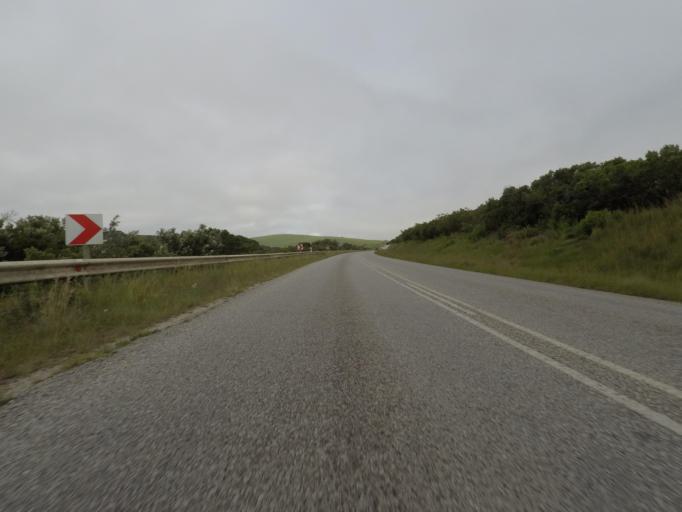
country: ZA
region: Eastern Cape
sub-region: Cacadu District Municipality
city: Port Alfred
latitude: -33.6100
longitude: 26.8094
